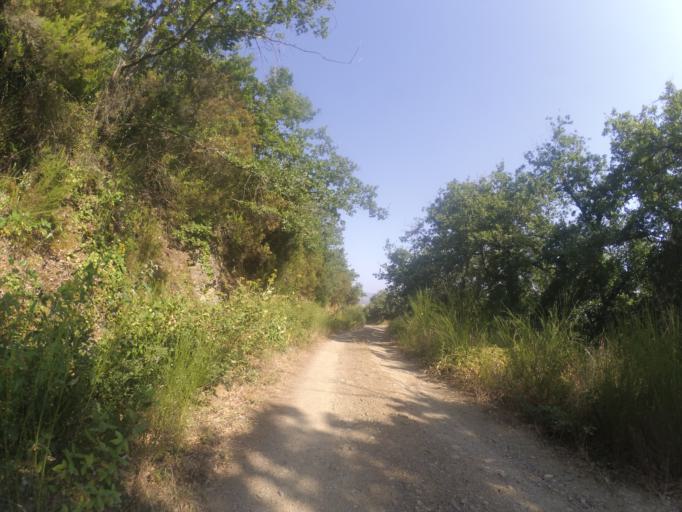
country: FR
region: Languedoc-Roussillon
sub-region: Departement des Pyrenees-Orientales
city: Ille-sur-Tet
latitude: 42.6498
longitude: 2.6339
